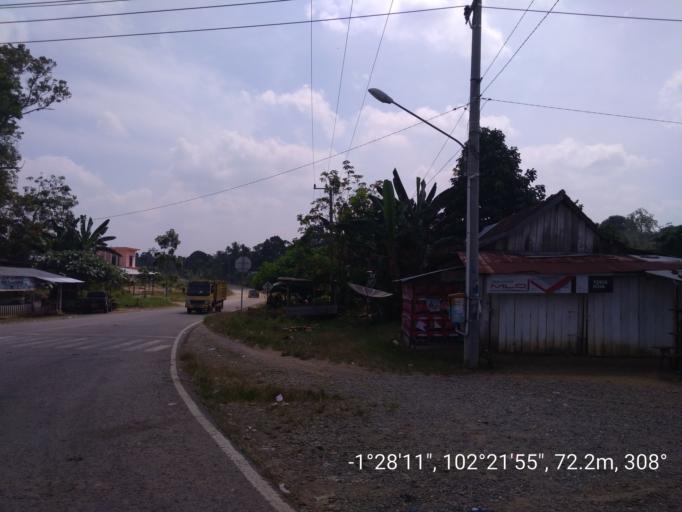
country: ID
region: Jambi
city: Muara Tebo
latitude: -1.4697
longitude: 102.3654
